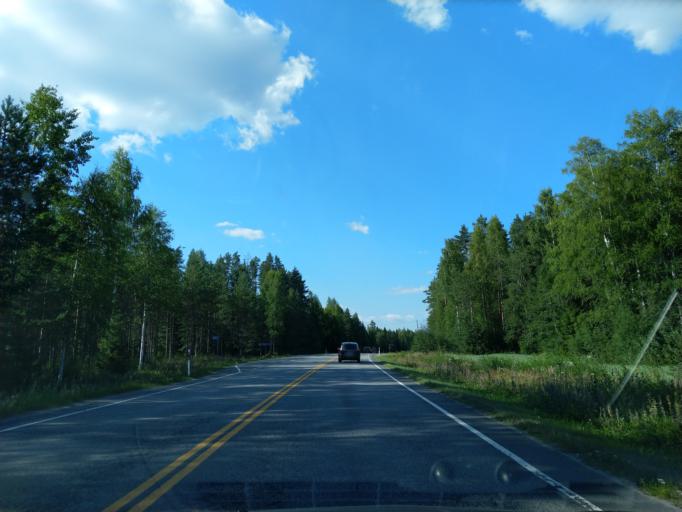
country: FI
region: Pirkanmaa
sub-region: Luoteis-Pirkanmaa
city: Kihnioe
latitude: 62.1653
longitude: 23.1617
